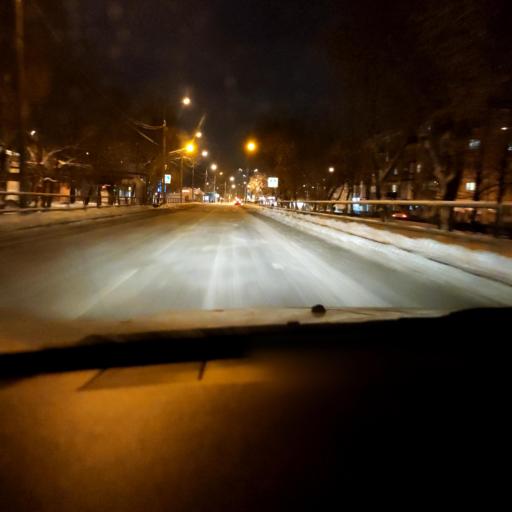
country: RU
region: Samara
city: Petra-Dubrava
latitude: 53.3005
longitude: 50.2847
